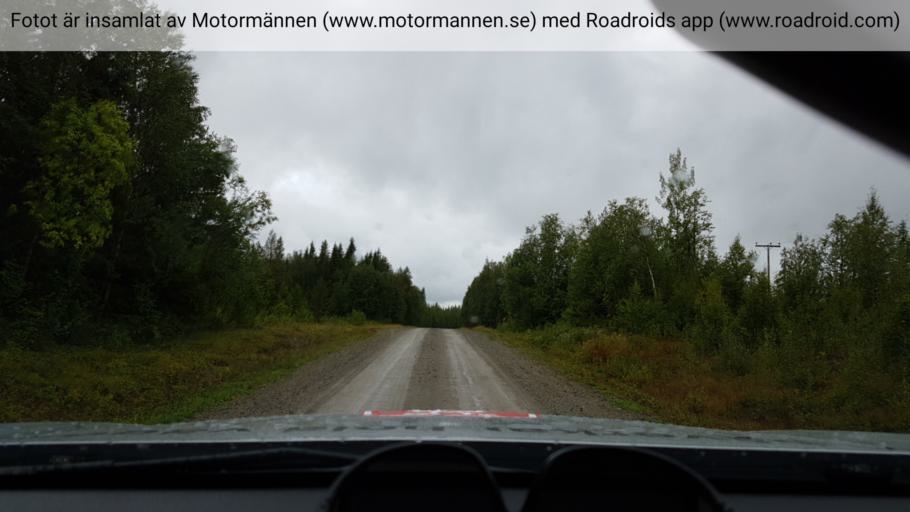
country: SE
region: Vaesterbotten
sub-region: Asele Kommun
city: Insjon
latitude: 64.7847
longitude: 17.5569
